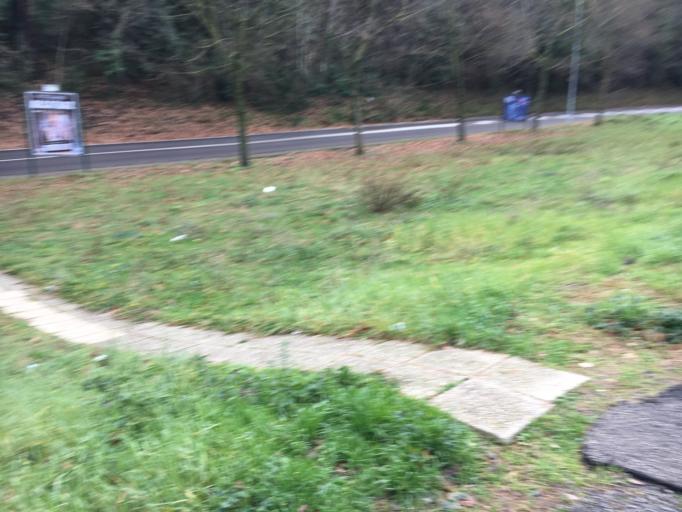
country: IT
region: Umbria
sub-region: Provincia di Perugia
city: Perugia
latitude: 43.1160
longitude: 12.3747
